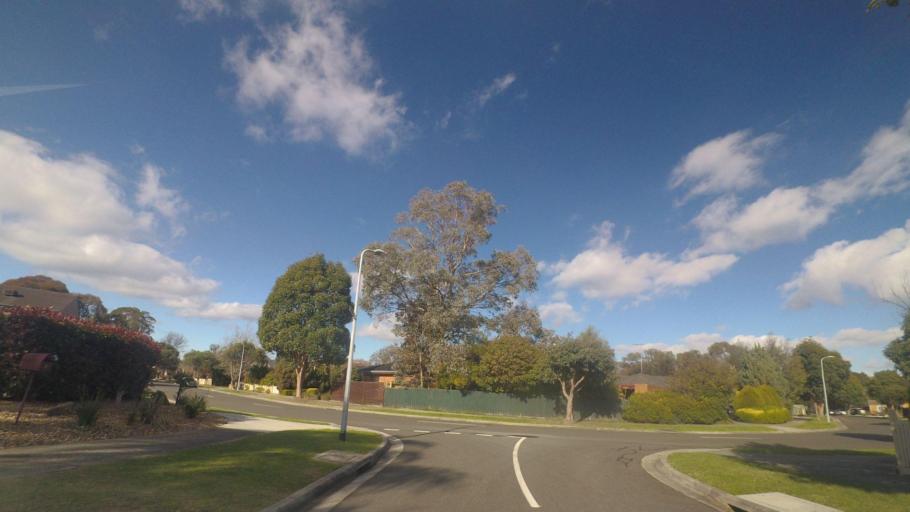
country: AU
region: Victoria
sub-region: Knox
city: Rowville
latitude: -37.9291
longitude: 145.2361
